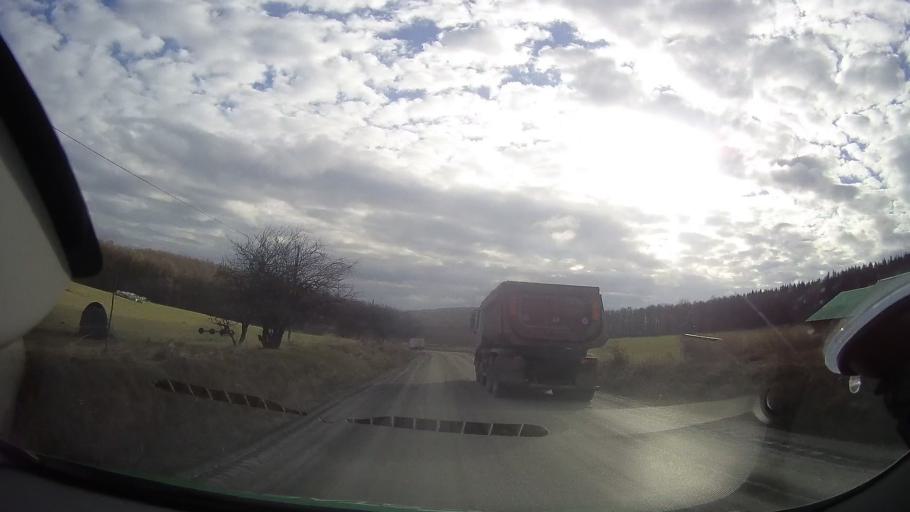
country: RO
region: Cluj
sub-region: Comuna Savadisla
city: Savadisla
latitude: 46.6487
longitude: 23.4614
